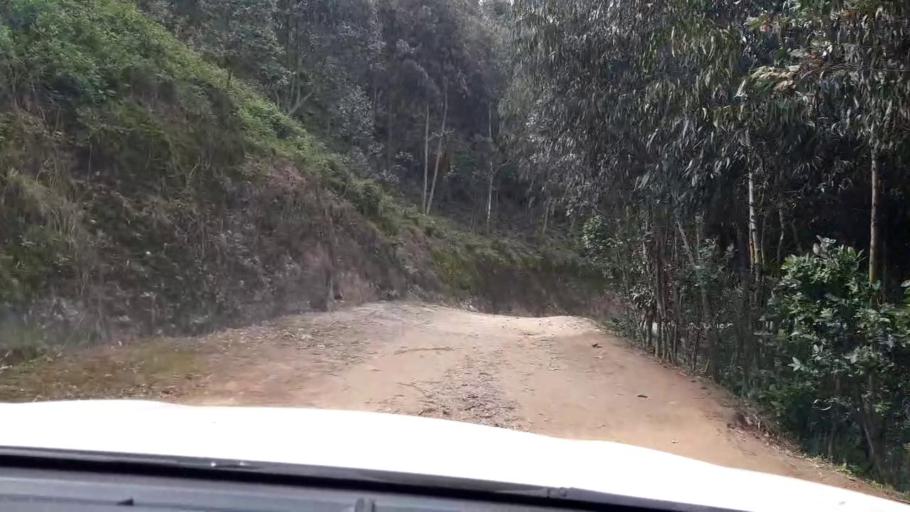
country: RW
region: Western Province
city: Kibuye
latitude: -1.8772
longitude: 29.4535
